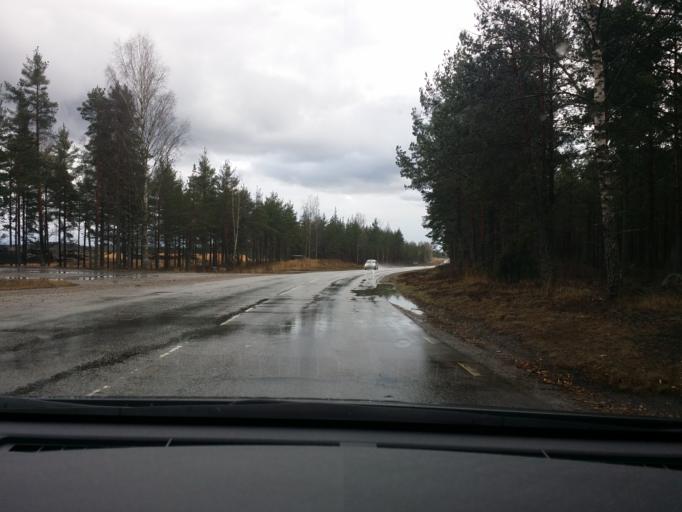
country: SE
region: Soedermanland
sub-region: Eskilstuna Kommun
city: Arla
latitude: 59.3398
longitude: 16.6912
